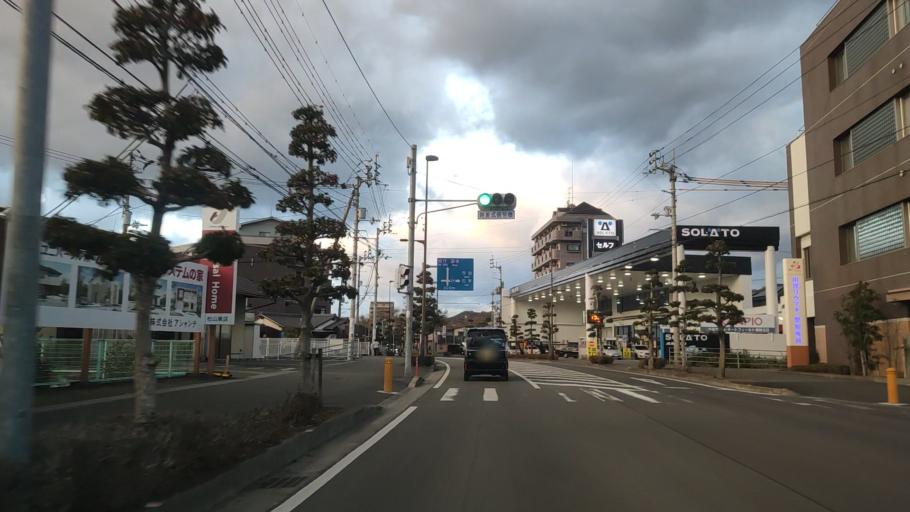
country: JP
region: Ehime
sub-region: Shikoku-chuo Shi
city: Matsuyama
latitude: 33.8373
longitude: 132.7868
